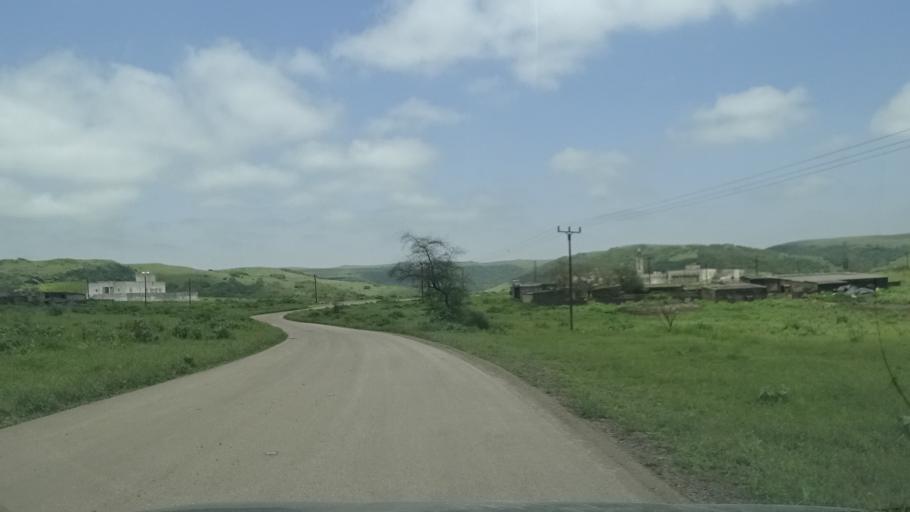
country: OM
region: Zufar
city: Salalah
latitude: 17.2102
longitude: 54.1915
